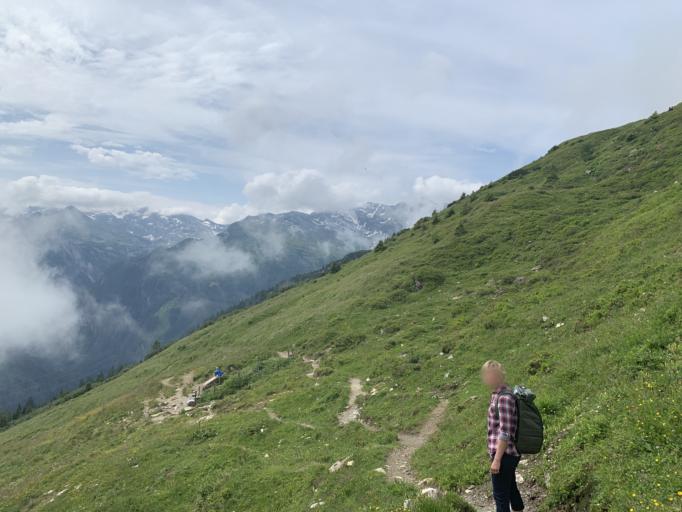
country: AT
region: Salzburg
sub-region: Politischer Bezirk Sankt Johann im Pongau
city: Bad Gastein
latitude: 47.1117
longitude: 13.1062
